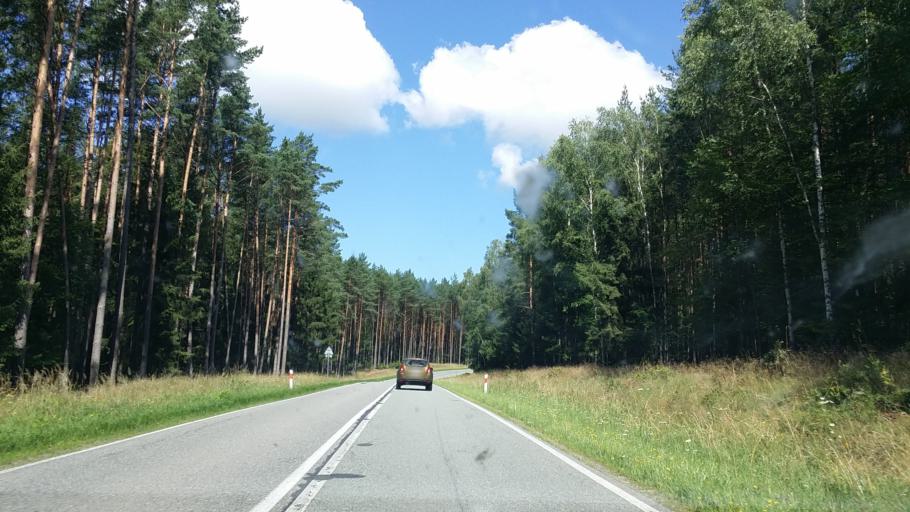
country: PL
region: West Pomeranian Voivodeship
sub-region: Powiat drawski
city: Drawsko Pomorskie
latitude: 53.4145
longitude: 15.8312
